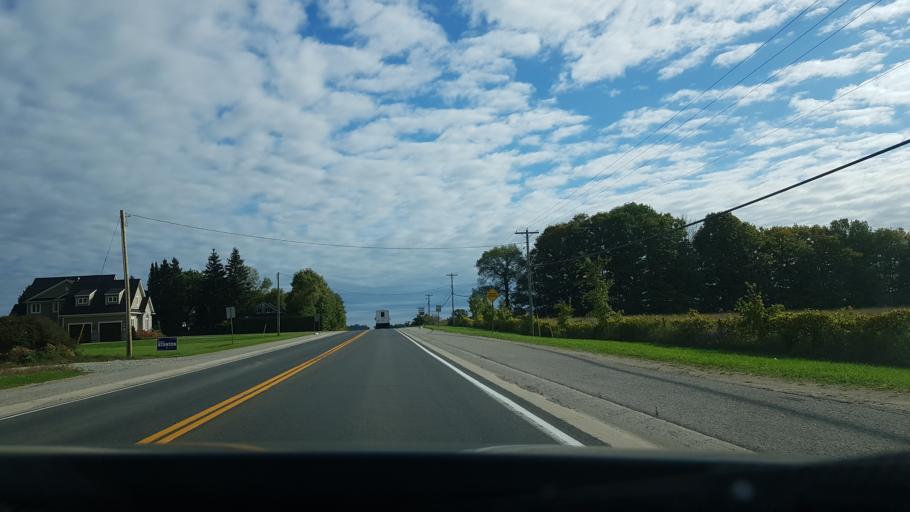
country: CA
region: Ontario
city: Orillia
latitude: 44.5968
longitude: -79.5680
